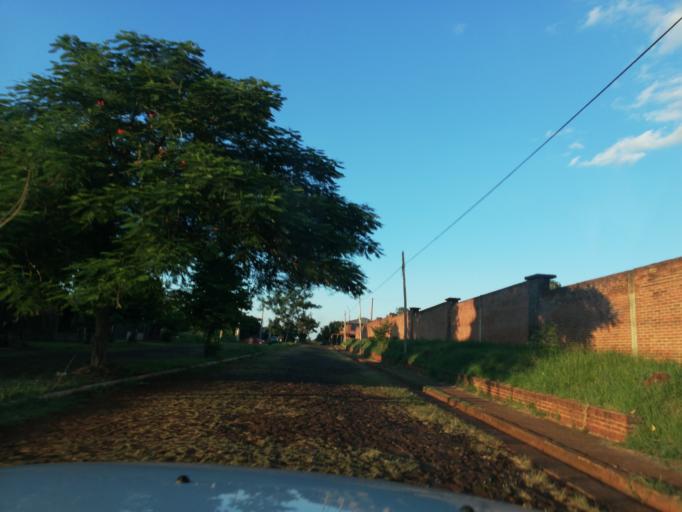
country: AR
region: Misiones
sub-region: Departamento de Capital
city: Posadas
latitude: -27.3833
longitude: -55.9491
